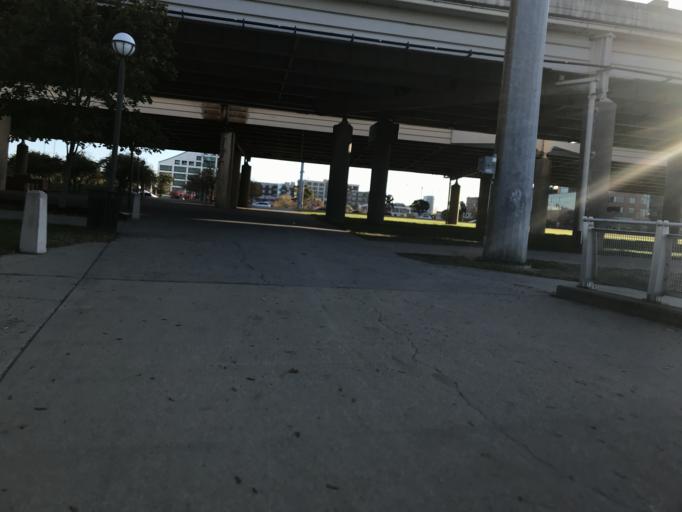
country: US
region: Kentucky
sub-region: Jefferson County
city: Louisville
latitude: 38.2591
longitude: -85.7462
